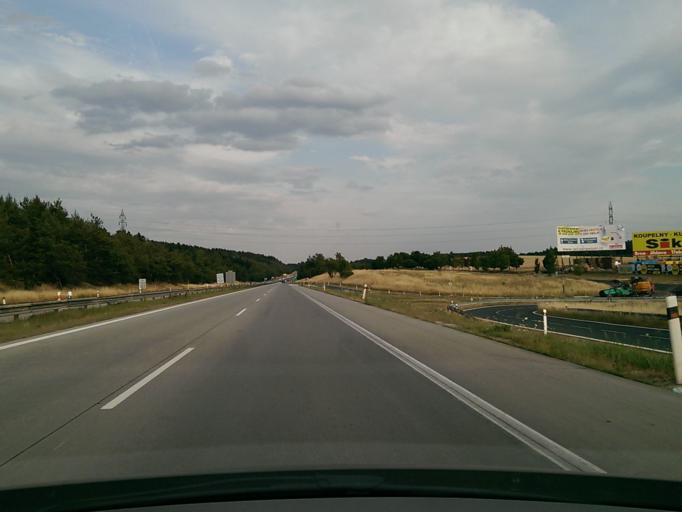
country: CZ
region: Vysocina
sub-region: Okres Zd'ar nad Sazavou
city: Velke Mezirici
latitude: 49.3455
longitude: 16.0436
